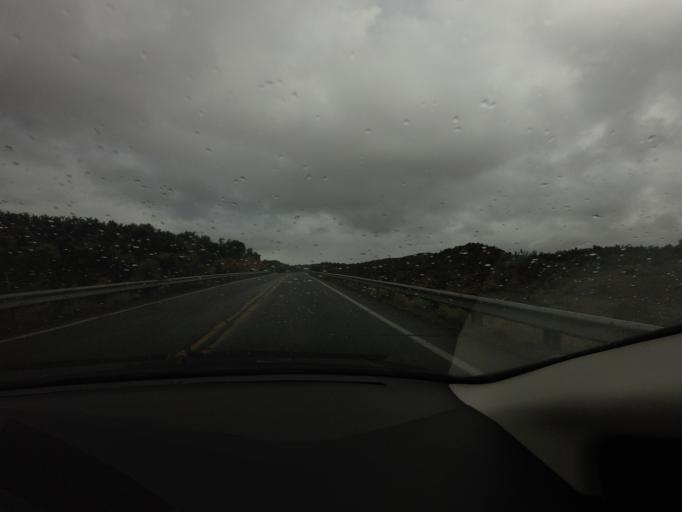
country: US
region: Arizona
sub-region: Yavapai County
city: Cornville
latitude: 34.7021
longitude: -111.8692
